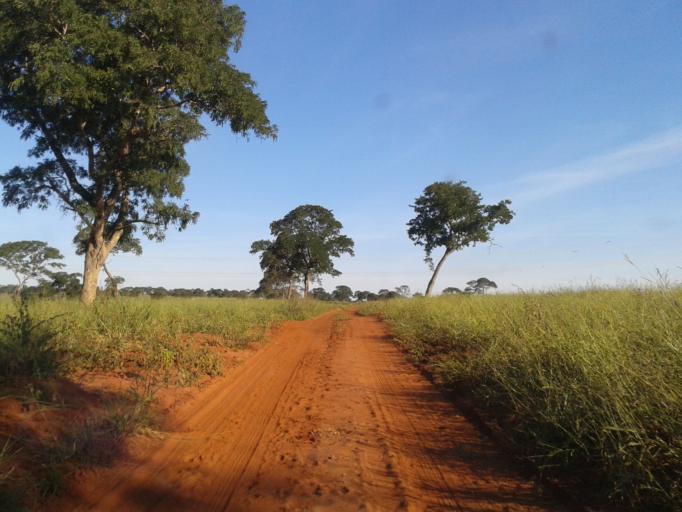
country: BR
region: Minas Gerais
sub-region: Santa Vitoria
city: Santa Vitoria
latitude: -19.0070
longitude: -50.3361
